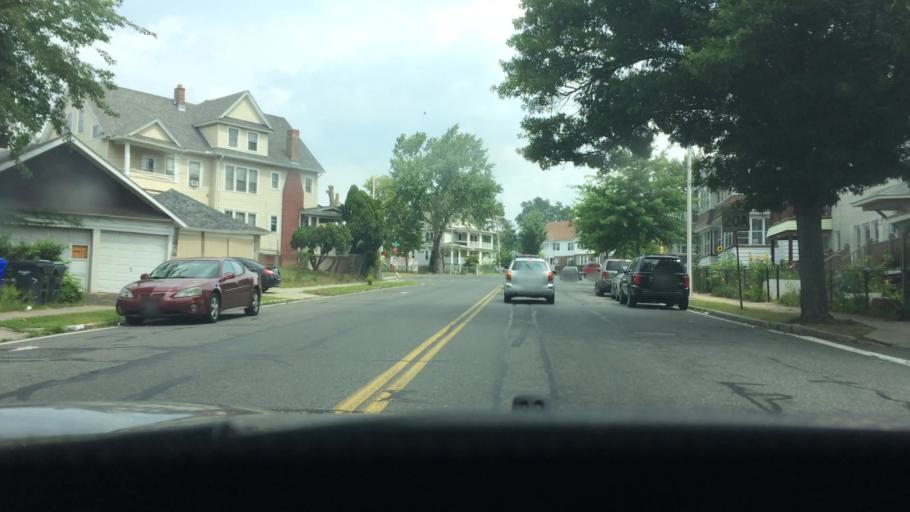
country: US
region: Massachusetts
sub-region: Hampden County
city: Springfield
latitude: 42.1182
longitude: -72.5948
